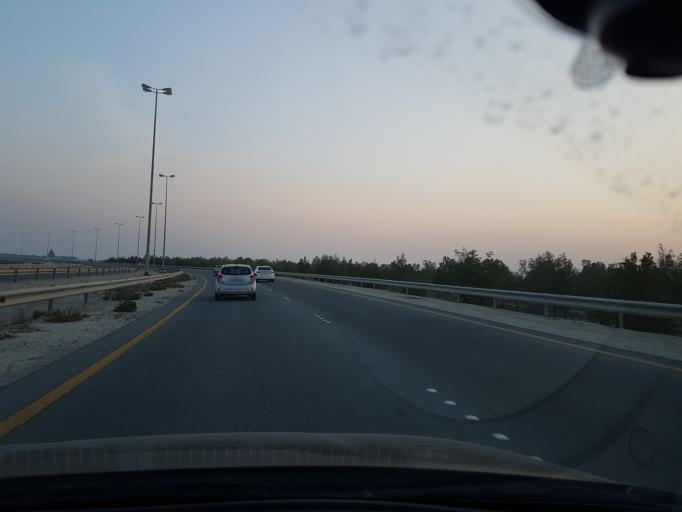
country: BH
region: Central Governorate
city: Dar Kulayb
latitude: 26.0145
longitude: 50.4845
